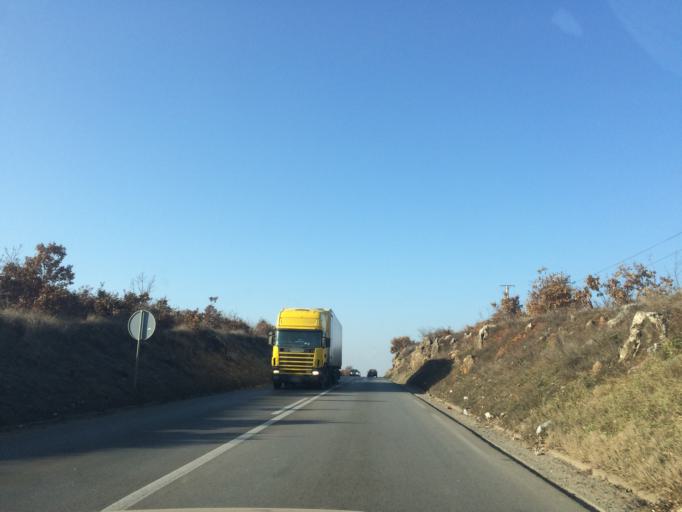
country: XK
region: Pec
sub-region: Komuna e Klines
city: Klina
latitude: 42.5952
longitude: 20.6466
